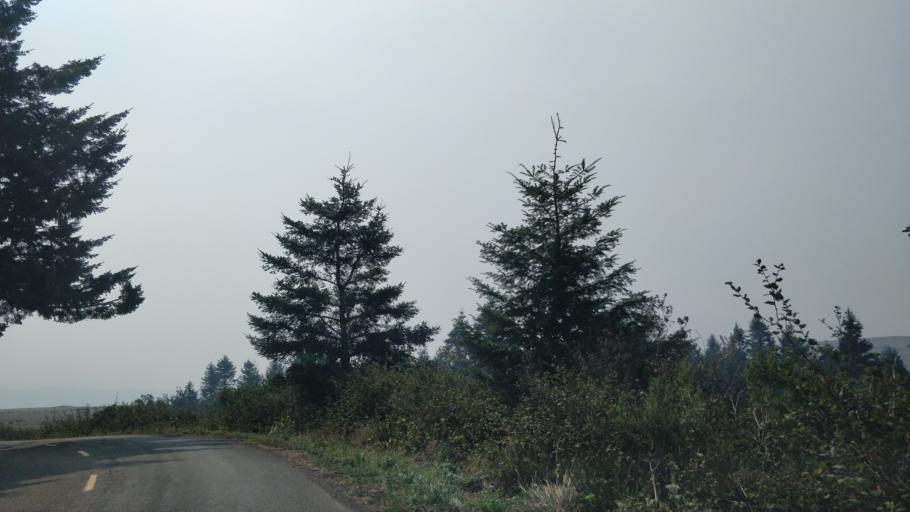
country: US
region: California
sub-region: Humboldt County
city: Ferndale
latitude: 40.4919
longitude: -124.3265
